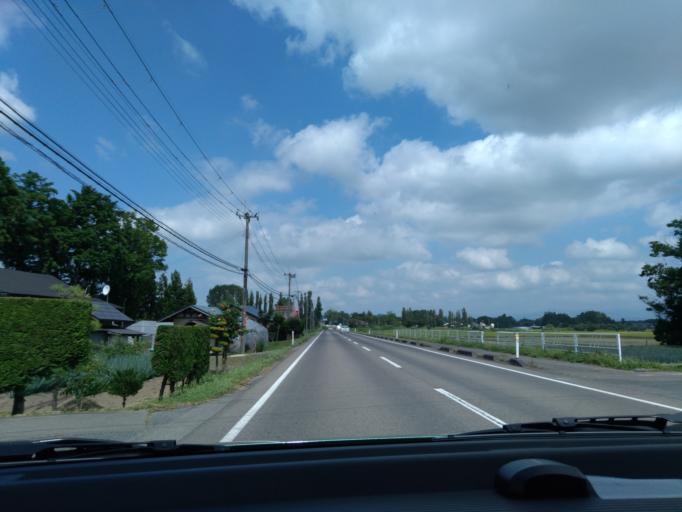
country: JP
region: Iwate
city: Hanamaki
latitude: 39.4540
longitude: 141.0987
